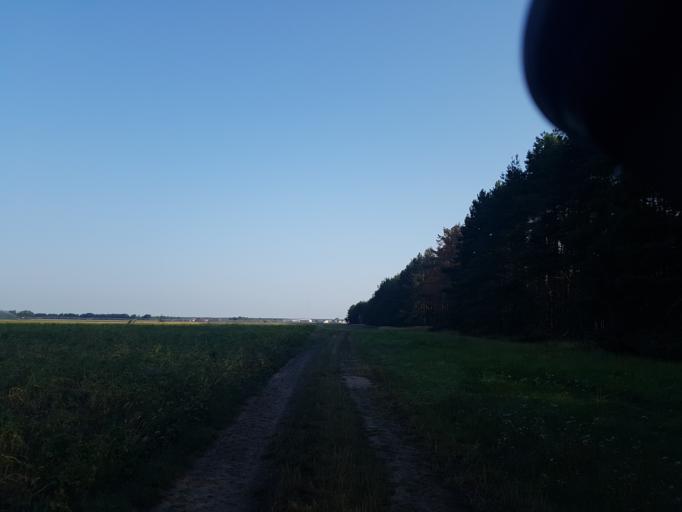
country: DE
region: Saxony-Anhalt
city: Holzdorf
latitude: 51.8389
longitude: 13.1163
